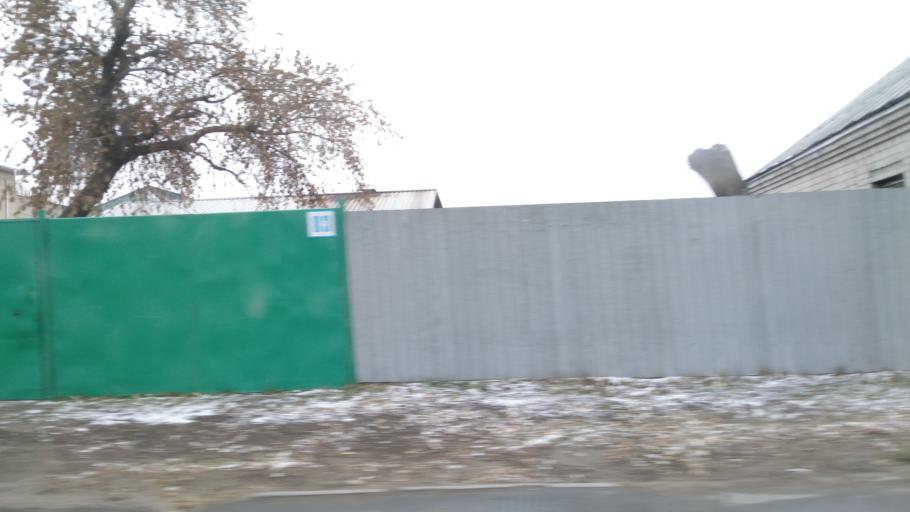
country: KZ
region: Pavlodar
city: Pavlodar
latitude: 52.2755
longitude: 76.9583
